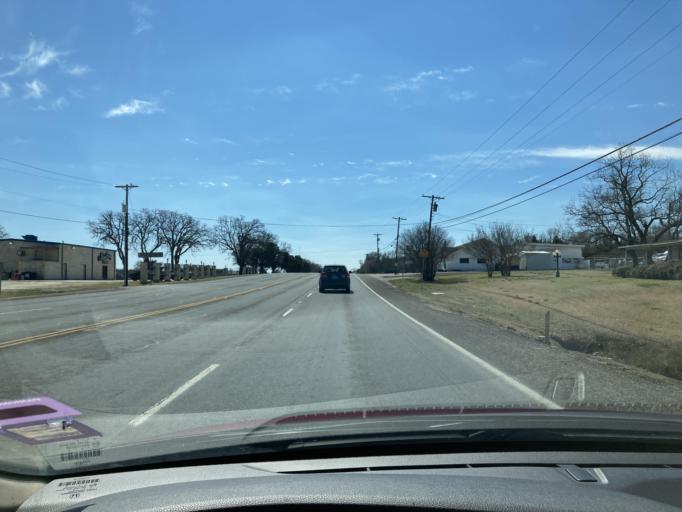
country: US
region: Texas
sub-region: Navarro County
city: Corsicana
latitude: 32.1223
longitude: -96.4655
